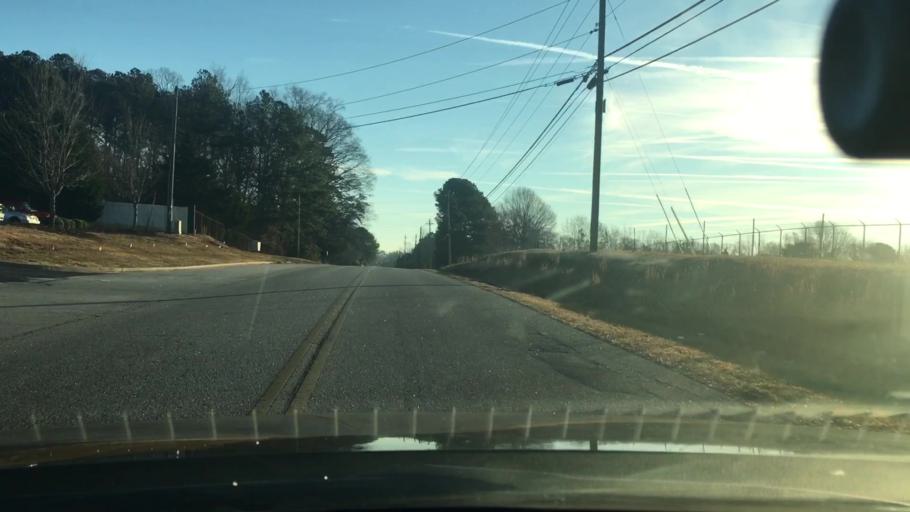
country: US
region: Georgia
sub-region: Spalding County
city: Experiment
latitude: 33.2610
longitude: -84.2951
